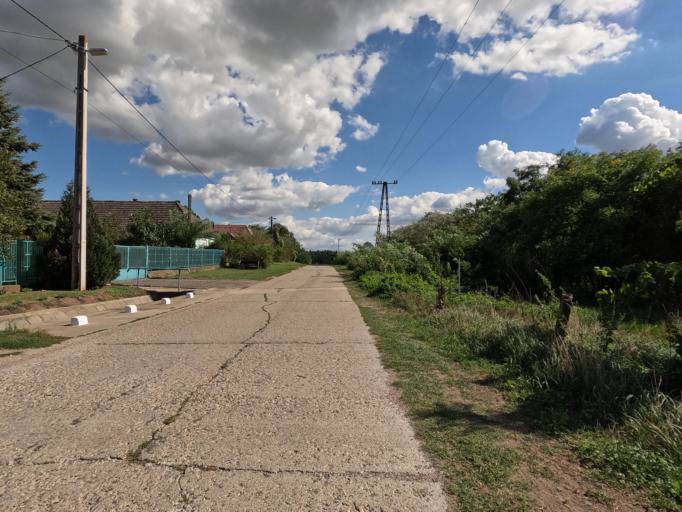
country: HU
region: Tolna
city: Paks
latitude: 46.5854
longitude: 18.8207
